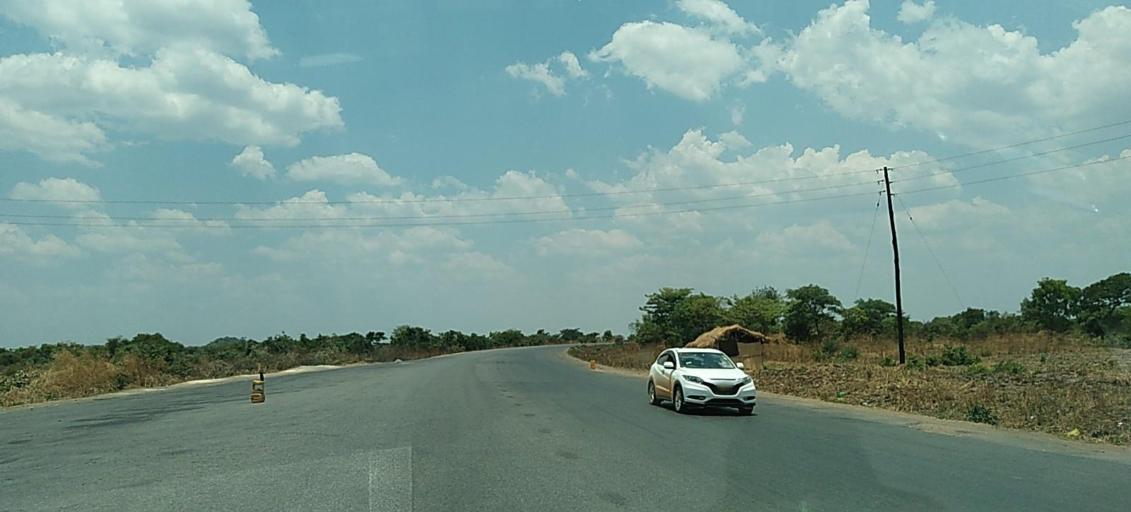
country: ZM
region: Central
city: Kapiri Mposhi
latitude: -13.8929
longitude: 28.6602
